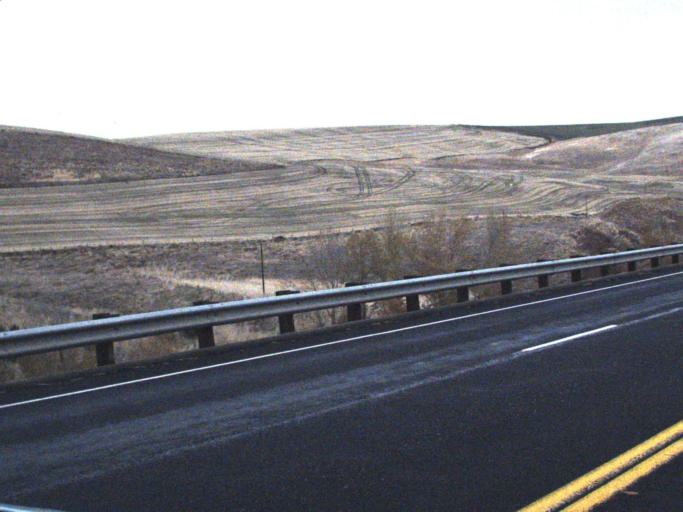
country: US
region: Washington
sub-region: Columbia County
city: Dayton
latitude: 46.4188
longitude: -117.9462
